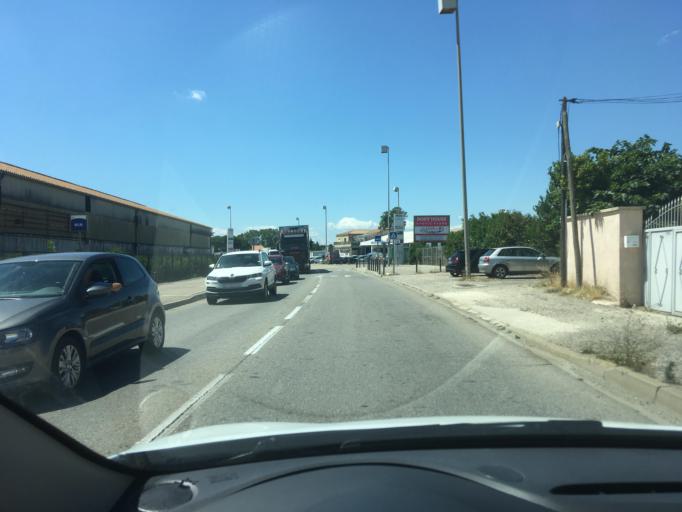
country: FR
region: Provence-Alpes-Cote d'Azur
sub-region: Departement des Bouches-du-Rhone
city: Chateaurenard
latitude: 43.8873
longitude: 4.8587
